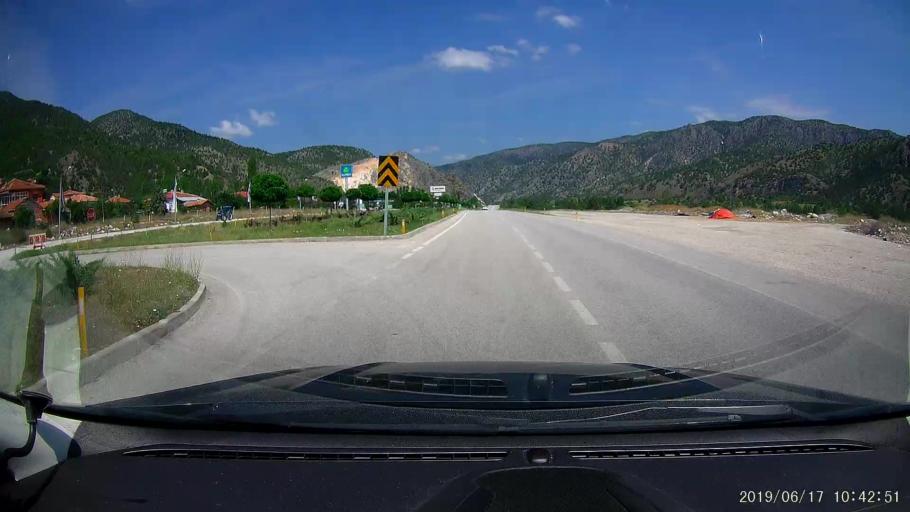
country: TR
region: Corum
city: Hacihamza
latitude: 41.0539
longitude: 34.5457
